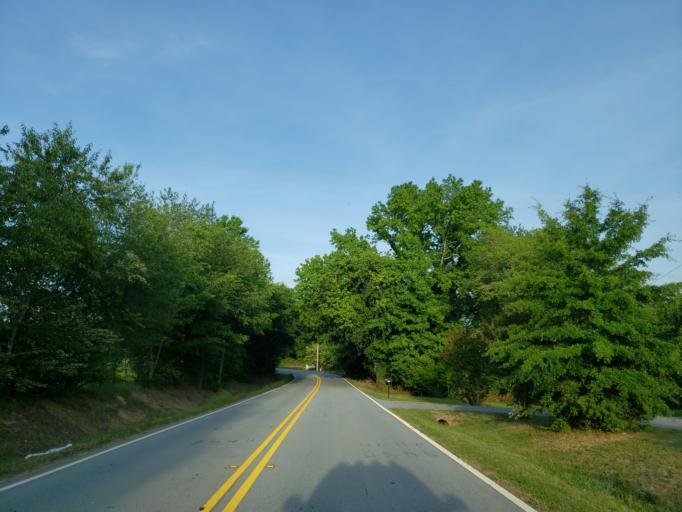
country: US
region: Georgia
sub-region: Carroll County
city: Mount Zion
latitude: 33.6104
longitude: -85.1660
